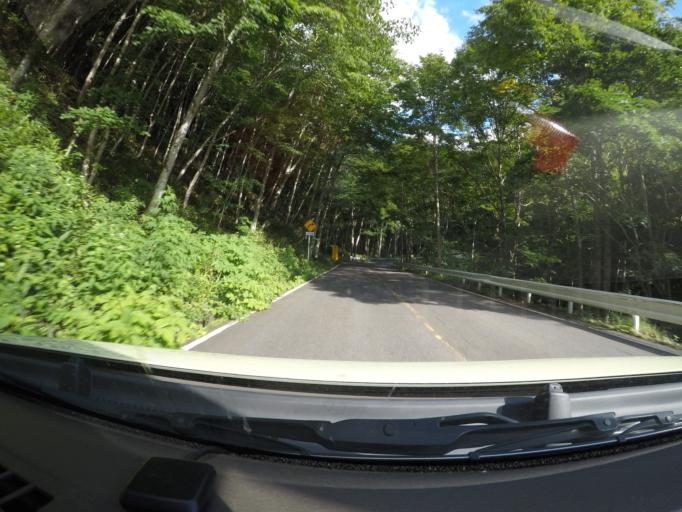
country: JP
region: Tochigi
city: Nikko
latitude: 36.8197
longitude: 139.3460
